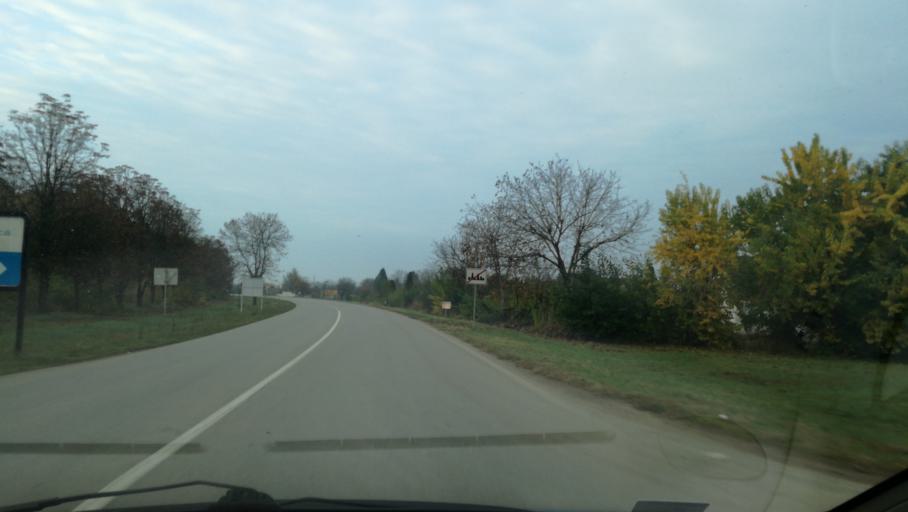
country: RS
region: Autonomna Pokrajina Vojvodina
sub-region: Severnobanatski Okrug
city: Kikinda
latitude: 45.8144
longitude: 20.4340
